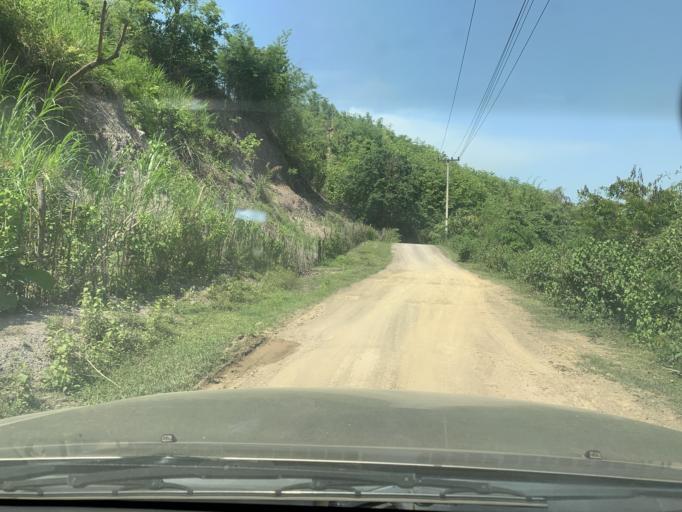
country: LA
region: Louangphabang
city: Louangphabang
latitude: 19.9123
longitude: 102.2604
